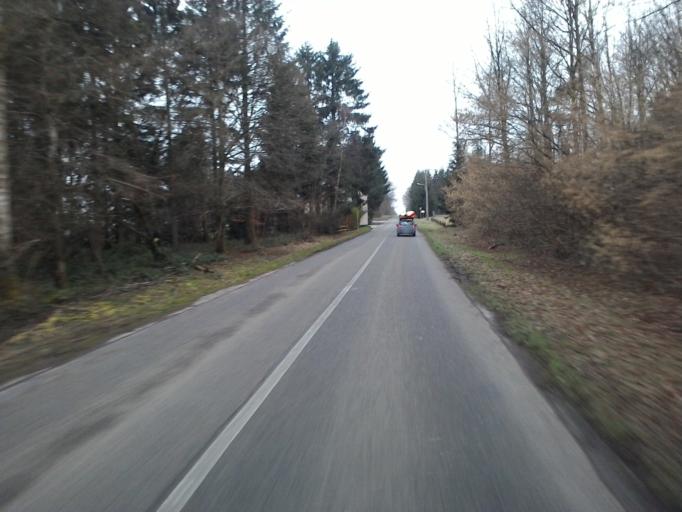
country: BE
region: Wallonia
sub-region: Province de Namur
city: Gedinne
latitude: 50.0377
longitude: 4.9541
